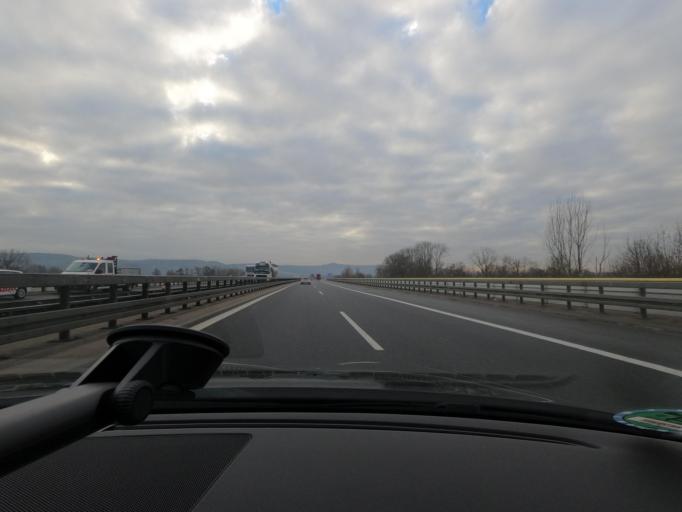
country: DE
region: Bavaria
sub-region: Upper Franconia
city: Lichtenfels
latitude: 50.1399
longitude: 11.0349
